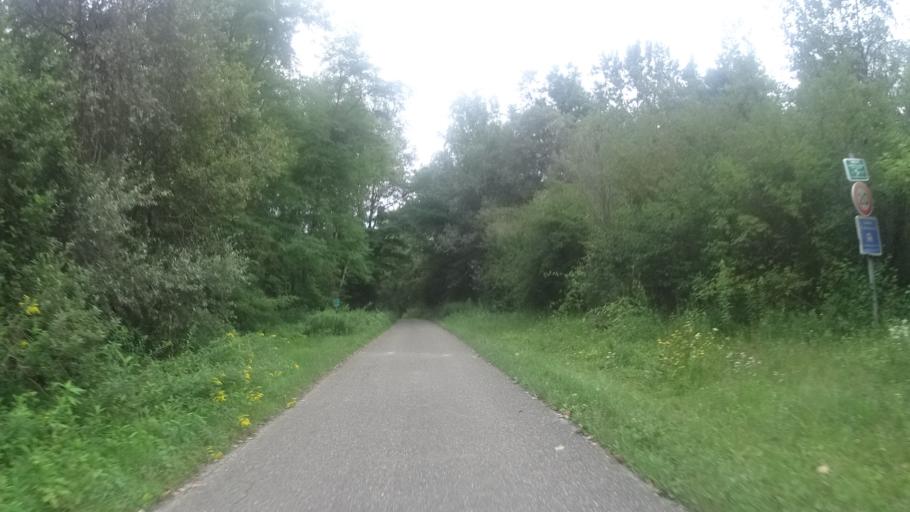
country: FR
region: Alsace
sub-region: Departement du Bas-Rhin
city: Seltz
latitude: 48.9018
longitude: 8.1351
